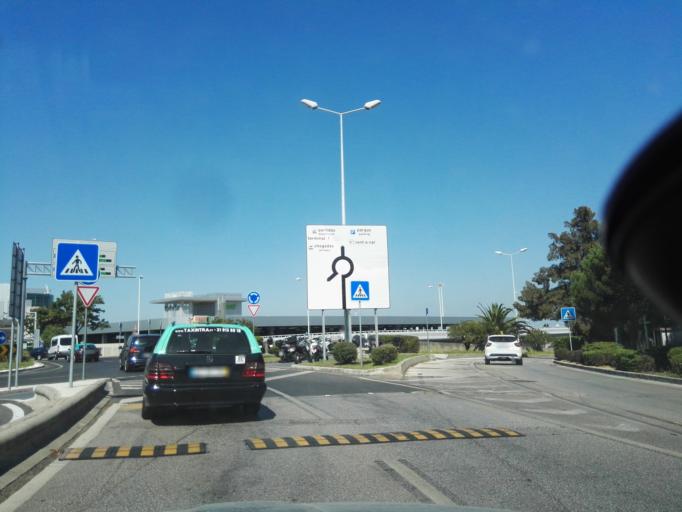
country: PT
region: Lisbon
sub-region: Loures
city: Moscavide
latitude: 38.7666
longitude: -9.1290
